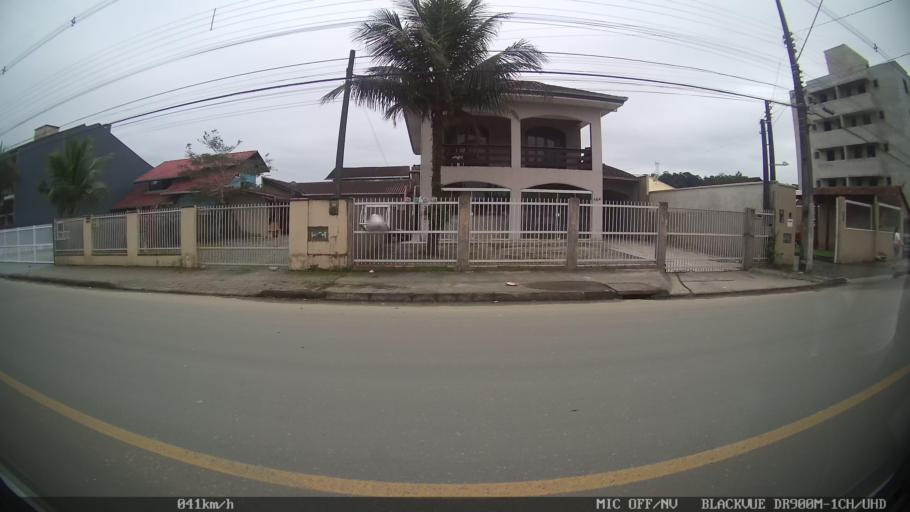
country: BR
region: Santa Catarina
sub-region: Joinville
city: Joinville
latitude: -26.2773
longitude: -48.9044
